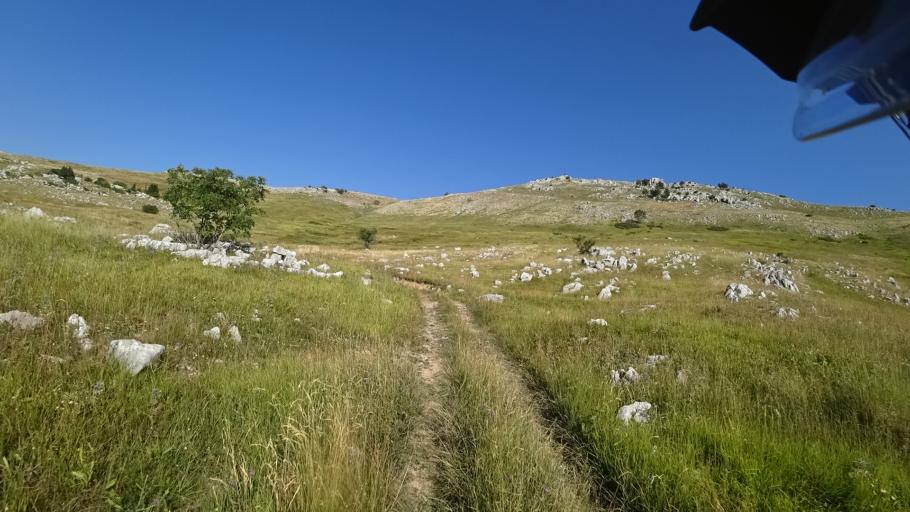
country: HR
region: Sibensko-Kniniska
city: Knin
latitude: 44.2048
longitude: 16.1501
